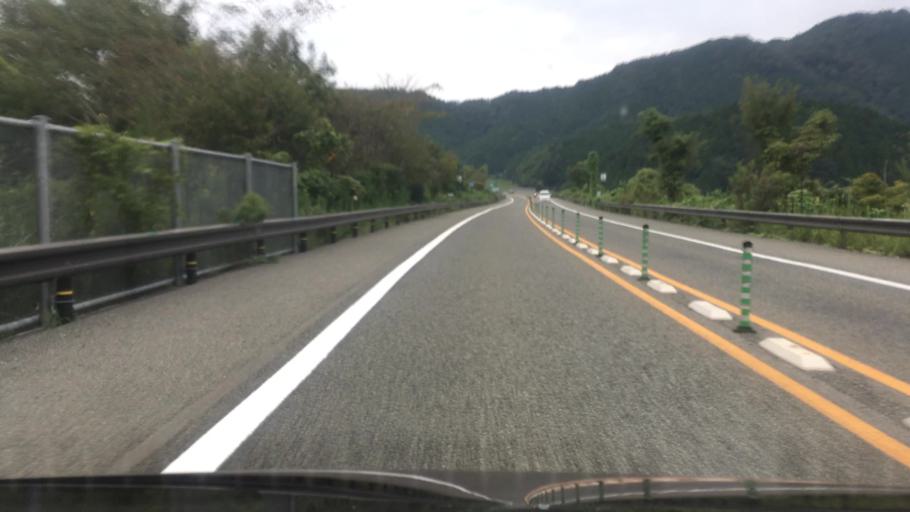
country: JP
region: Kyoto
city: Fukuchiyama
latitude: 35.3072
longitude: 134.8783
